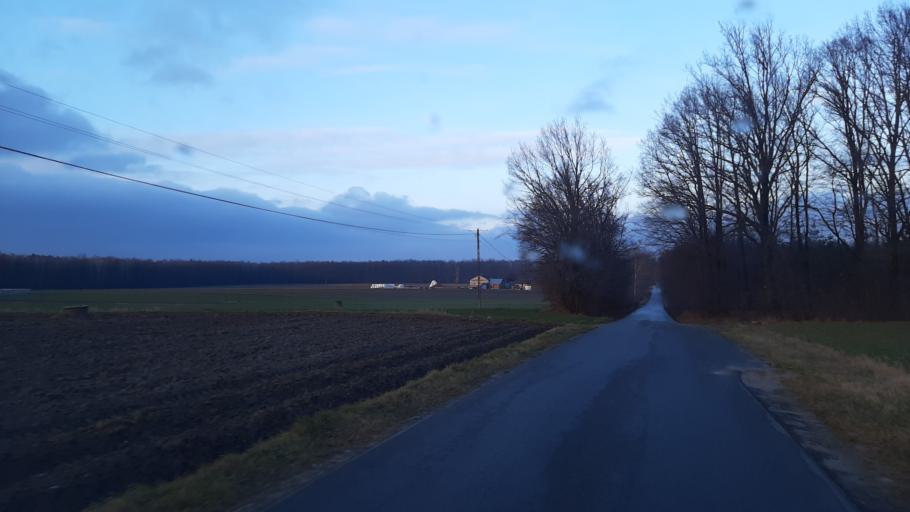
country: PL
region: Lublin Voivodeship
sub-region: Powiat lubelski
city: Garbow
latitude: 51.3680
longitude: 22.3986
